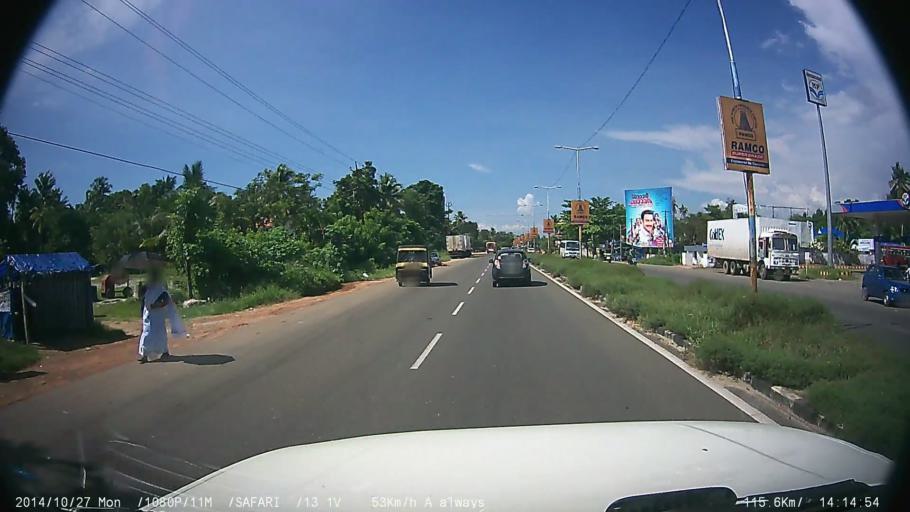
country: IN
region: Kerala
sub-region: Alappuzha
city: Kutiatodu
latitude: 9.8273
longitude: 76.3102
